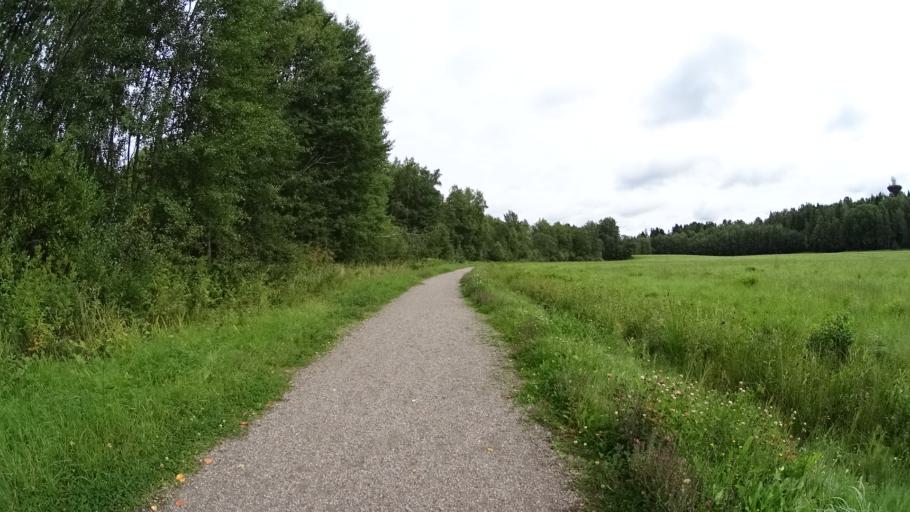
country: FI
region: Uusimaa
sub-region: Helsinki
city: Teekkarikylae
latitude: 60.2717
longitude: 24.8627
